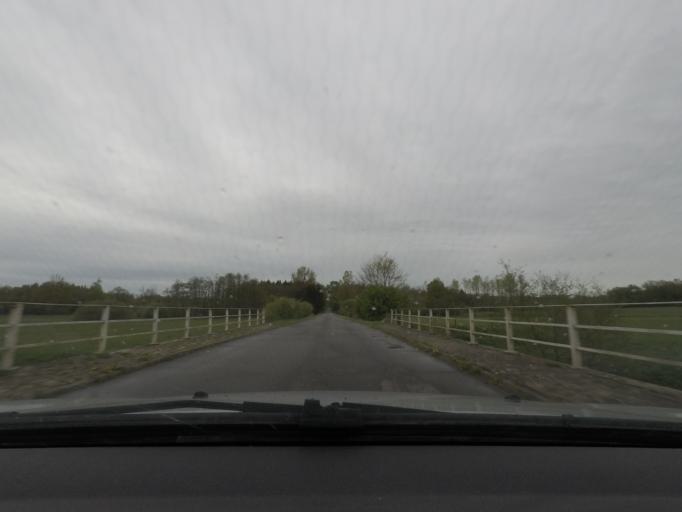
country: BE
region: Wallonia
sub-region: Province du Luxembourg
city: Etalle
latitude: 49.6849
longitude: 5.5637
